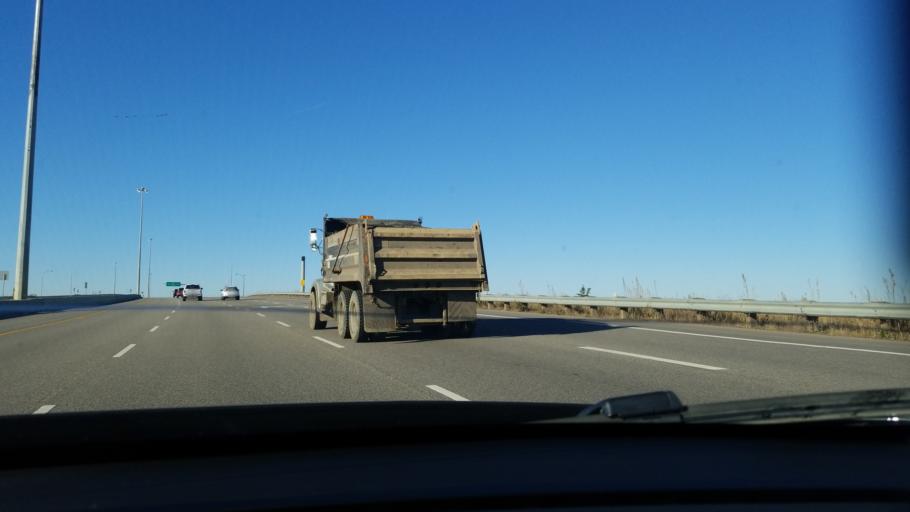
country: CA
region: Alberta
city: Sherwood Park
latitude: 53.4829
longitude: -113.3599
